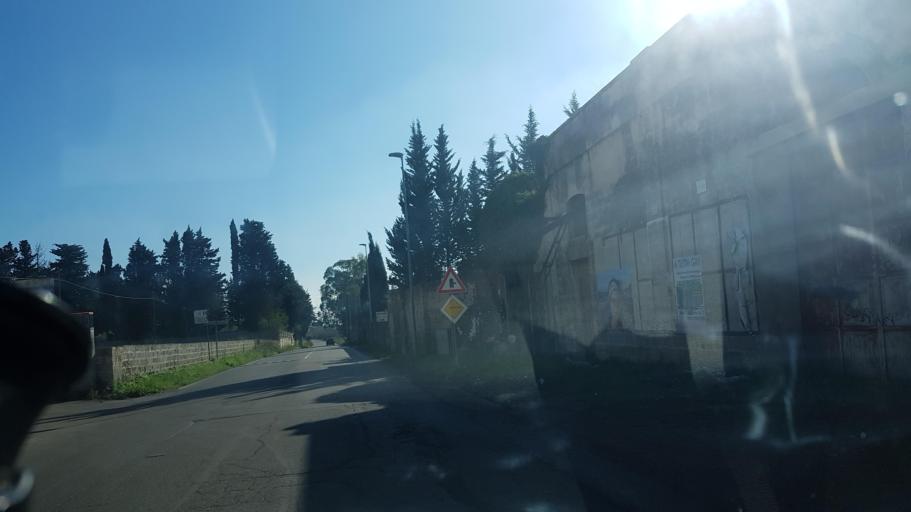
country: IT
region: Apulia
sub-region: Provincia di Lecce
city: Novoli
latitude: 40.3728
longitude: 18.0540
